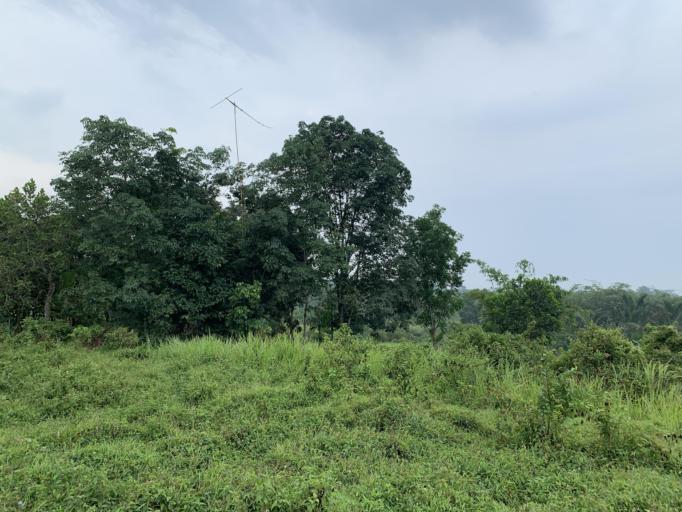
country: ID
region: West Java
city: Parung
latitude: -6.4314
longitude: 106.6253
